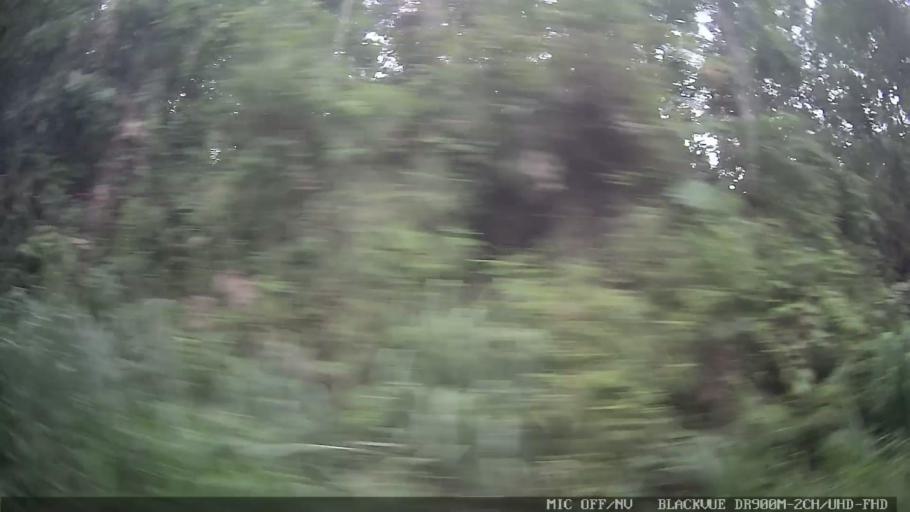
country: BR
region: Sao Paulo
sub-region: Biritiba-Mirim
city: Biritiba Mirim
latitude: -23.5443
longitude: -46.0862
